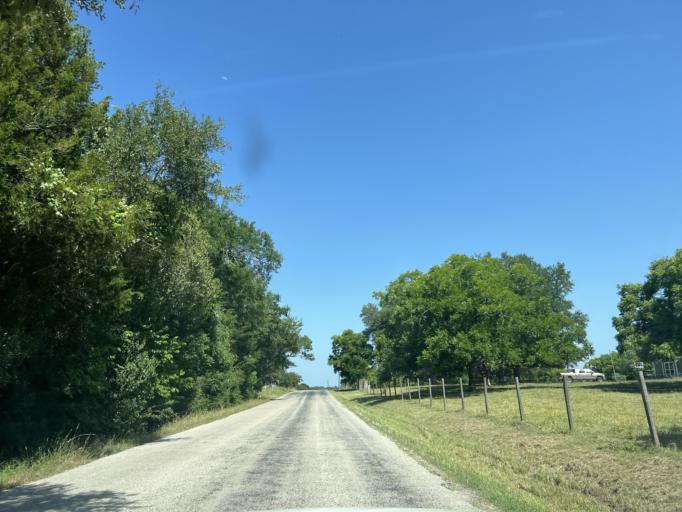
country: US
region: Texas
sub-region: Washington County
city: Brenham
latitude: 30.1756
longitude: -96.3491
